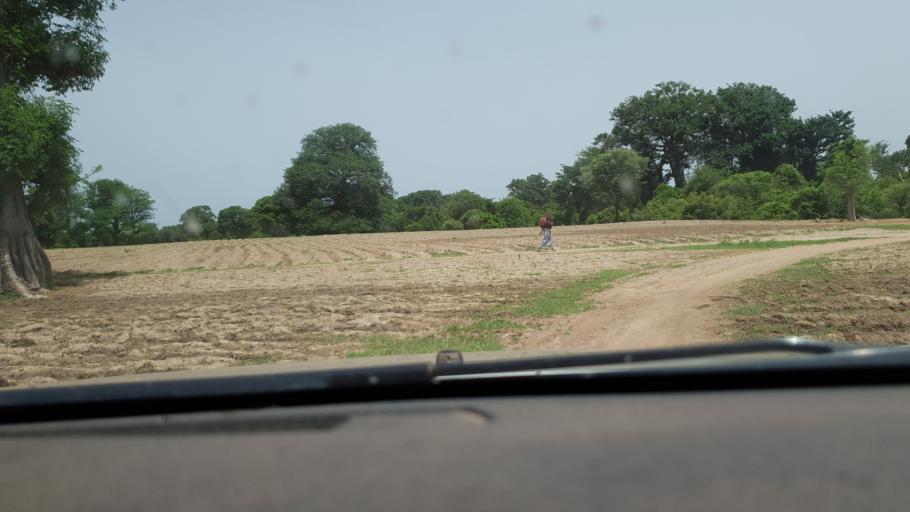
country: ML
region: Koulikoro
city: Koulikoro
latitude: 12.6681
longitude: -7.2439
